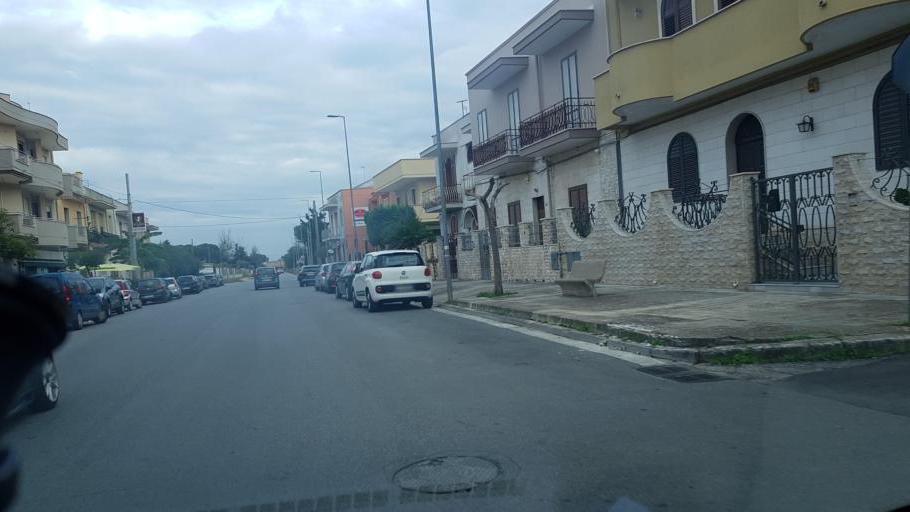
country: IT
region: Apulia
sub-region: Provincia di Brindisi
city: Francavilla Fontana
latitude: 40.5242
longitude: 17.5925
